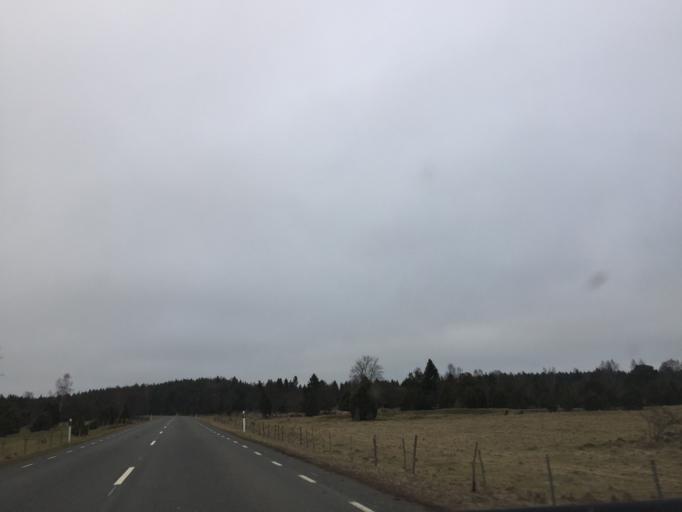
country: EE
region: Saare
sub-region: Kuressaare linn
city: Kuressaare
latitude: 58.5414
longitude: 22.3377
